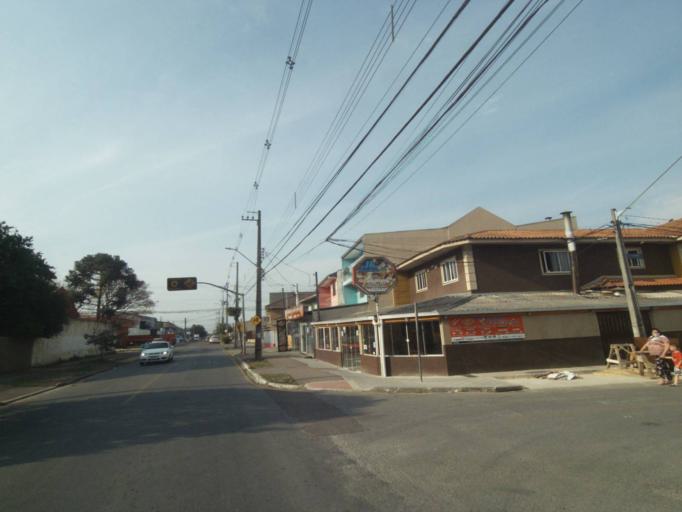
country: BR
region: Parana
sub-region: Pinhais
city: Pinhais
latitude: -25.4857
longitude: -49.2034
